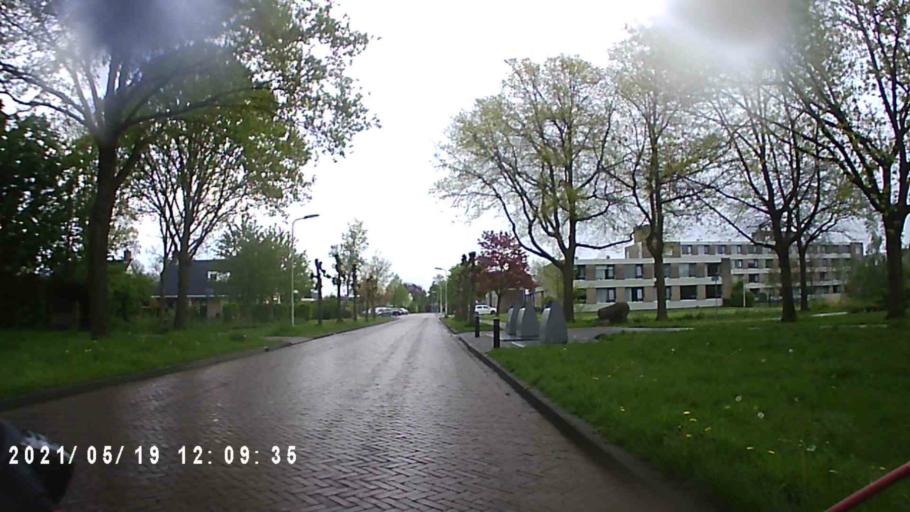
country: NL
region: Friesland
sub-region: Gemeente Achtkarspelen
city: Buitenpost
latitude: 53.2495
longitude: 6.1402
